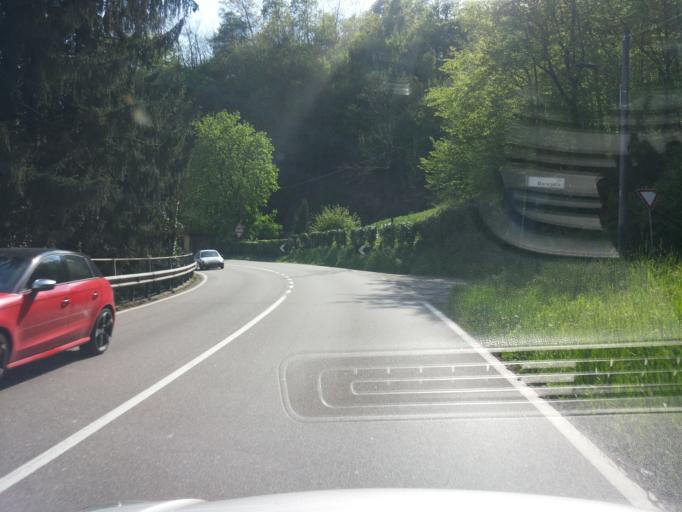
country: IT
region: Lombardy
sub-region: Provincia di Varese
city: Malnate
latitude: 45.8030
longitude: 8.8718
